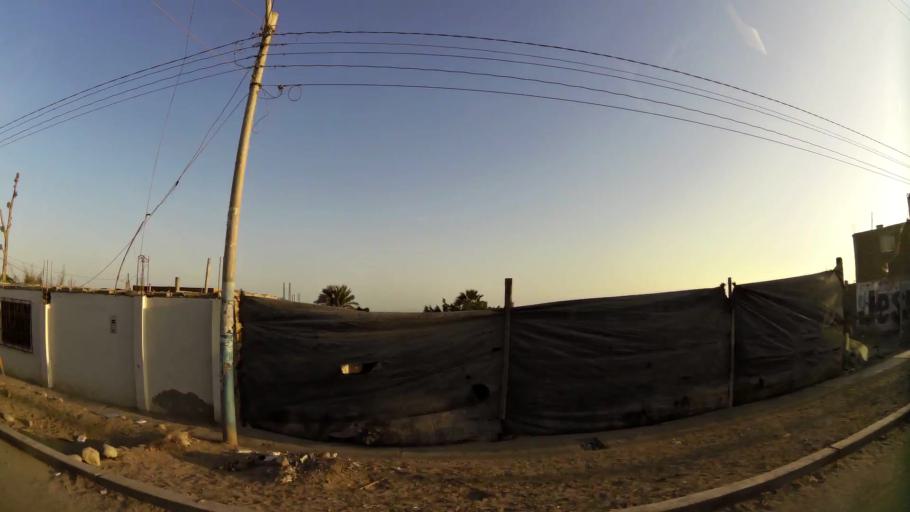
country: PE
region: Ica
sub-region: Provincia de Pisco
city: Villa Tupac Amaru
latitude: -13.7013
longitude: -76.1571
